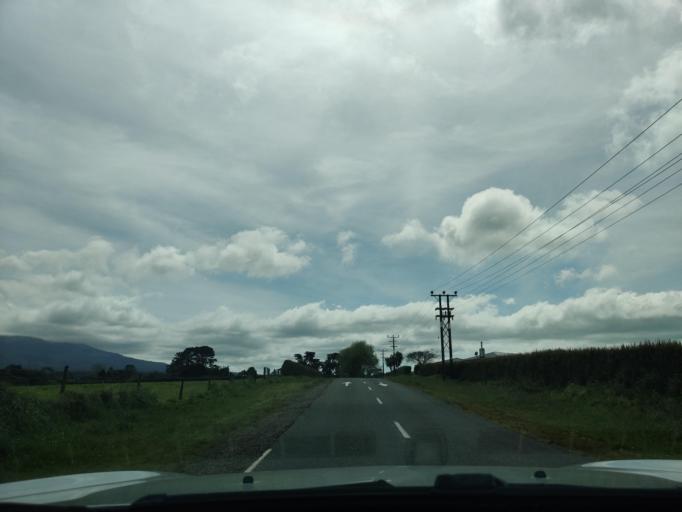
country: NZ
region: Taranaki
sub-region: South Taranaki District
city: Eltham
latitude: -39.3855
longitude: 174.1452
